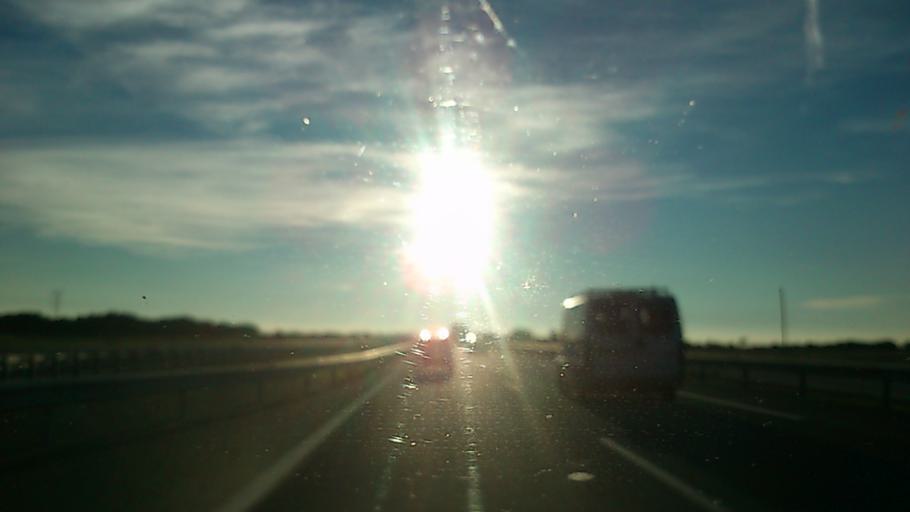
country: ES
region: Castille-La Mancha
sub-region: Provincia de Guadalajara
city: Utande
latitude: 40.8232
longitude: -2.9207
